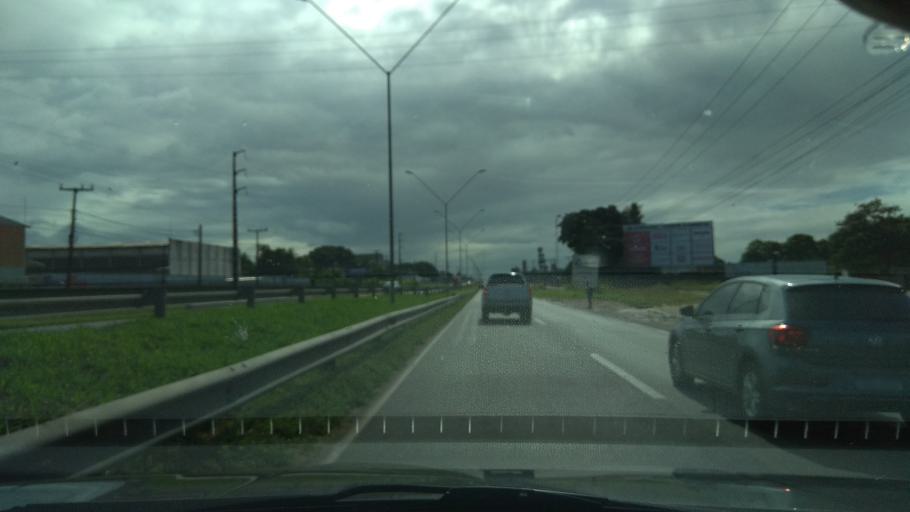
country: BR
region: Bahia
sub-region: Feira De Santana
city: Feira de Santana
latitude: -12.3077
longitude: -38.8883
